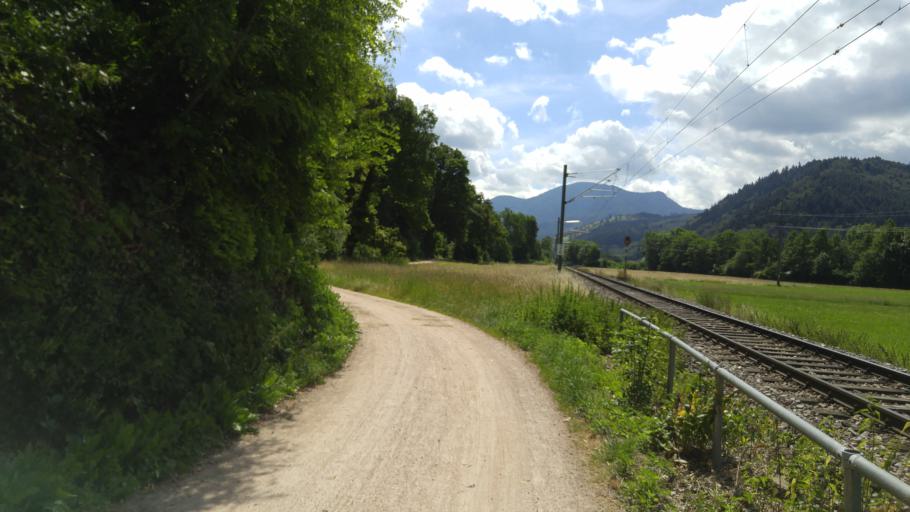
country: DE
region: Baden-Wuerttemberg
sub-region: Freiburg Region
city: Muenstertal/Schwarzwald
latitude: 47.8692
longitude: 7.7443
